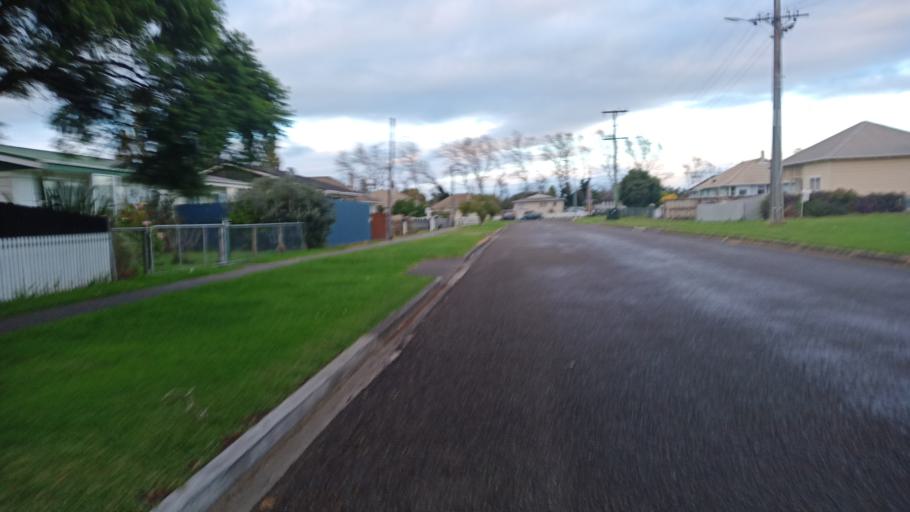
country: NZ
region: Gisborne
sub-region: Gisborne District
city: Gisborne
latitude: -38.6578
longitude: 177.9932
